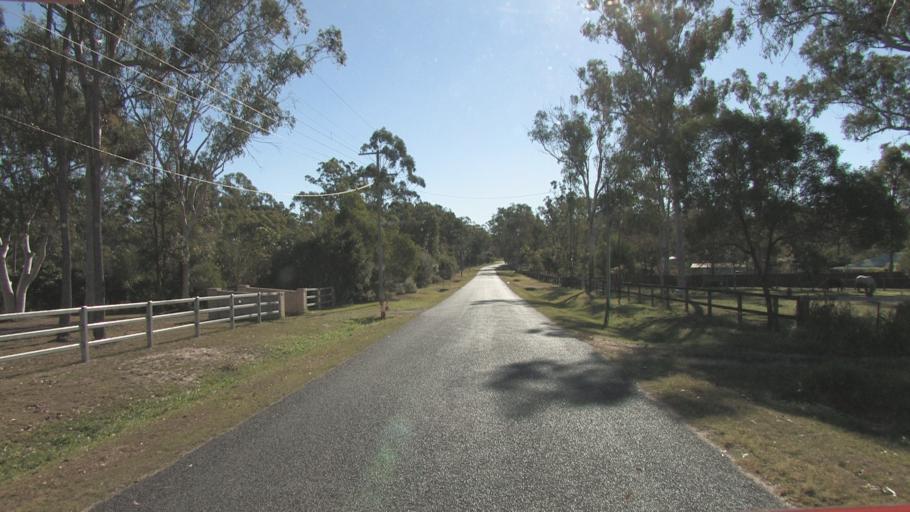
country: AU
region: Queensland
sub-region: Logan
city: Chambers Flat
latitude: -27.7423
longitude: 153.0812
